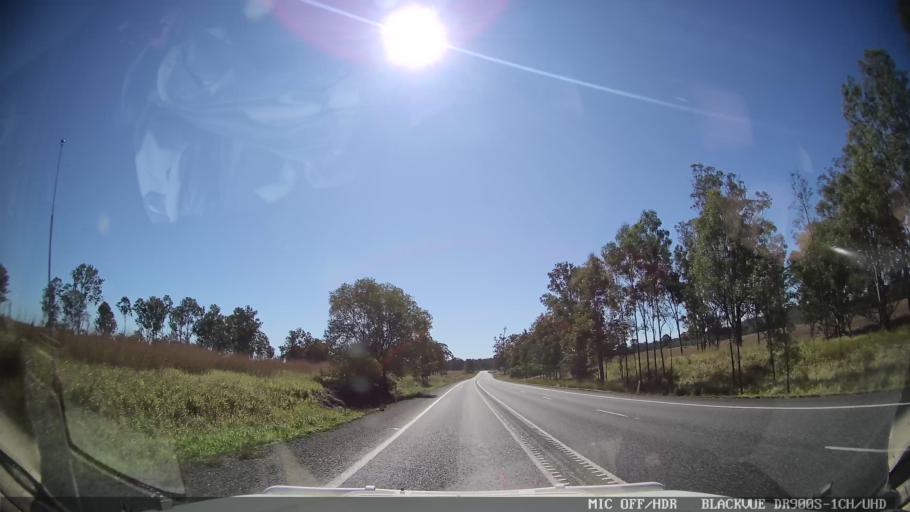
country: AU
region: Queensland
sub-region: Fraser Coast
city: Maryborough
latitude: -25.7713
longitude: 152.5967
